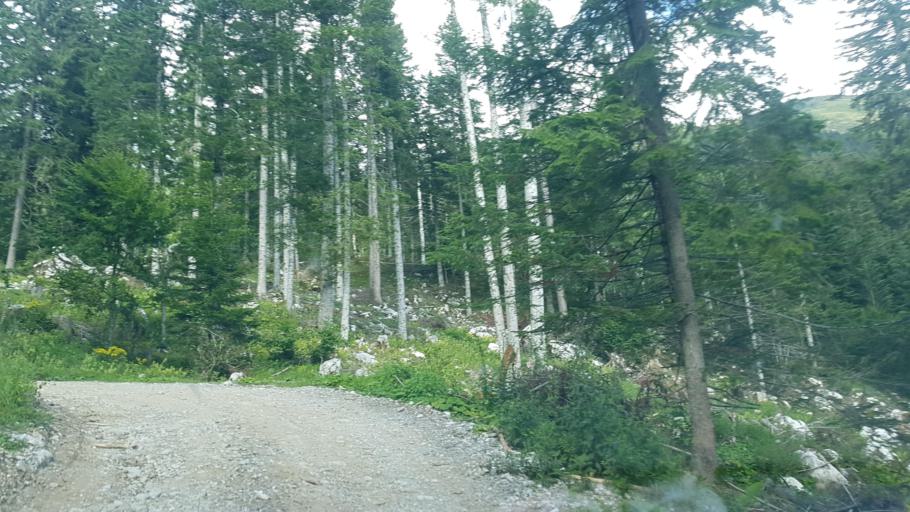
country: IT
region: Friuli Venezia Giulia
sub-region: Provincia di Udine
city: Forni Avoltri
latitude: 46.5890
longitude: 12.7972
